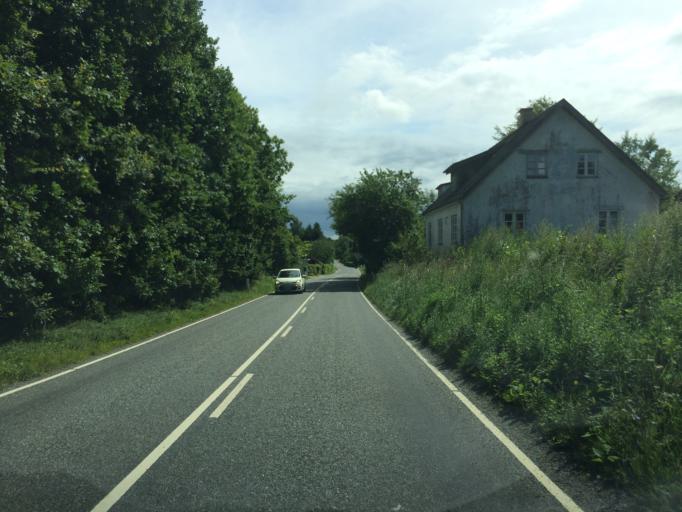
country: DK
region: South Denmark
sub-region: Faaborg-Midtfyn Kommune
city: Faaborg
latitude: 55.1743
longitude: 10.2549
